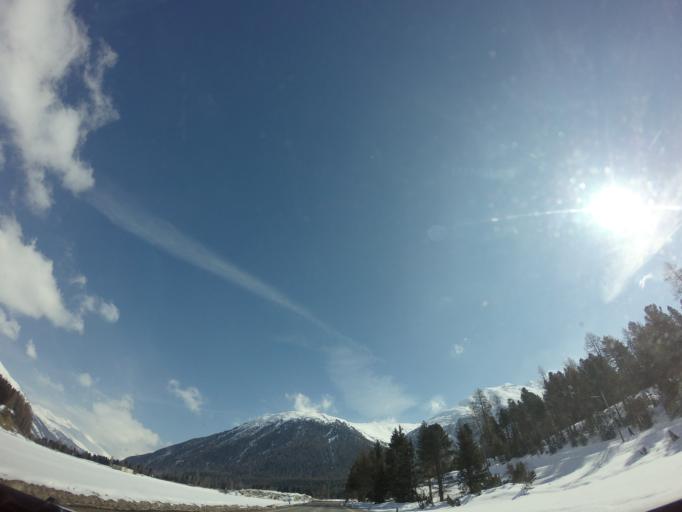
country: CH
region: Grisons
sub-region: Maloja District
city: Celerina
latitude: 46.5114
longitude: 9.8707
